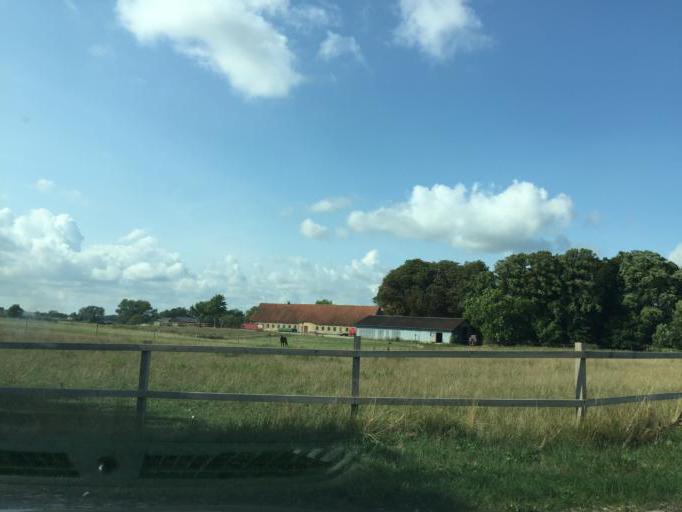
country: DK
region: South Denmark
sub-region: Odense Kommune
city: Bellinge
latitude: 55.3063
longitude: 10.3650
